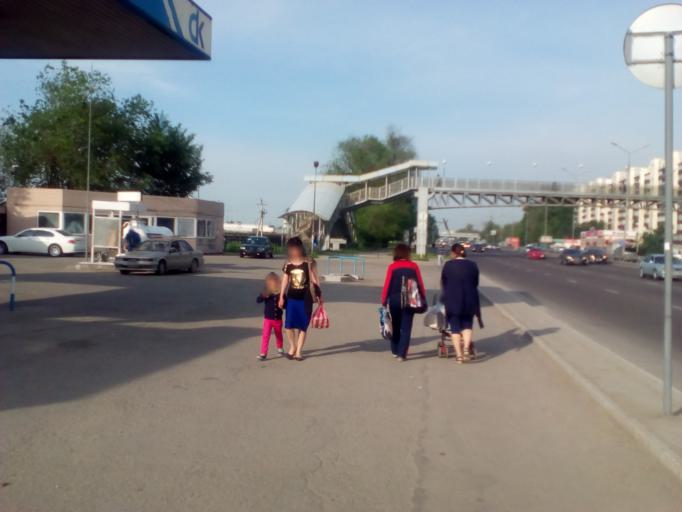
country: KZ
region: Almaty Qalasy
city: Almaty
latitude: 43.2418
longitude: 76.8205
